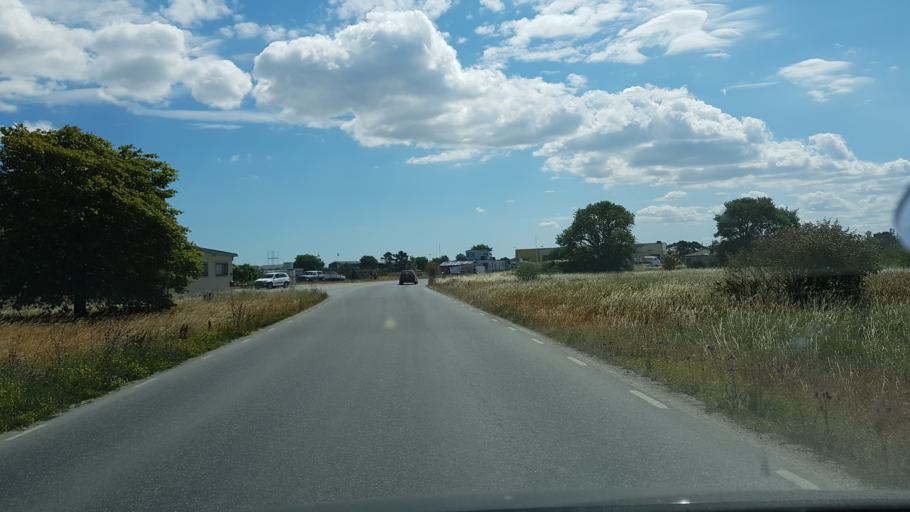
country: SE
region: Gotland
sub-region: Gotland
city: Visby
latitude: 57.6476
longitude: 18.3269
